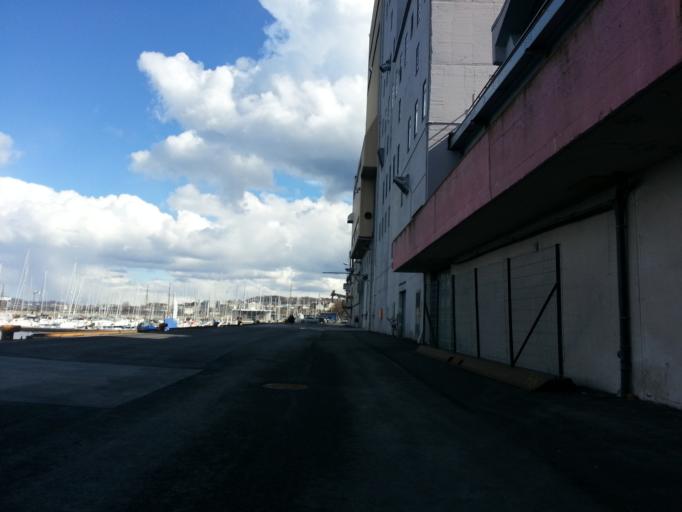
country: NO
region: Sor-Trondelag
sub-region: Trondheim
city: Trondheim
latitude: 63.4322
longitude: 10.3707
